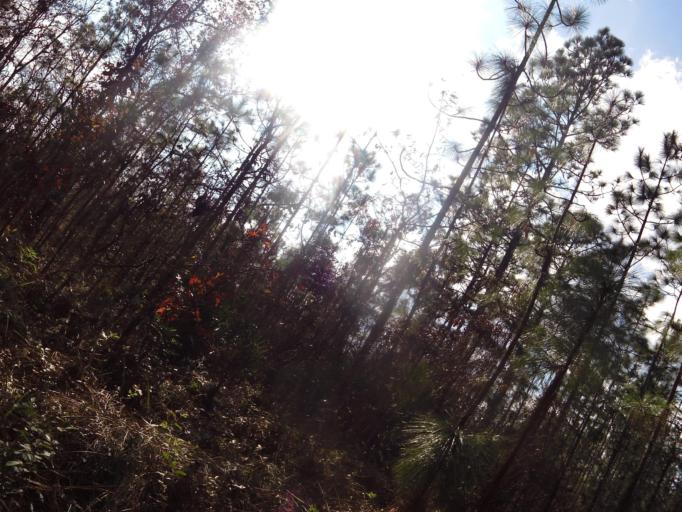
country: US
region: Florida
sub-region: Clay County
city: Middleburg
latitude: 30.1569
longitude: -81.9735
